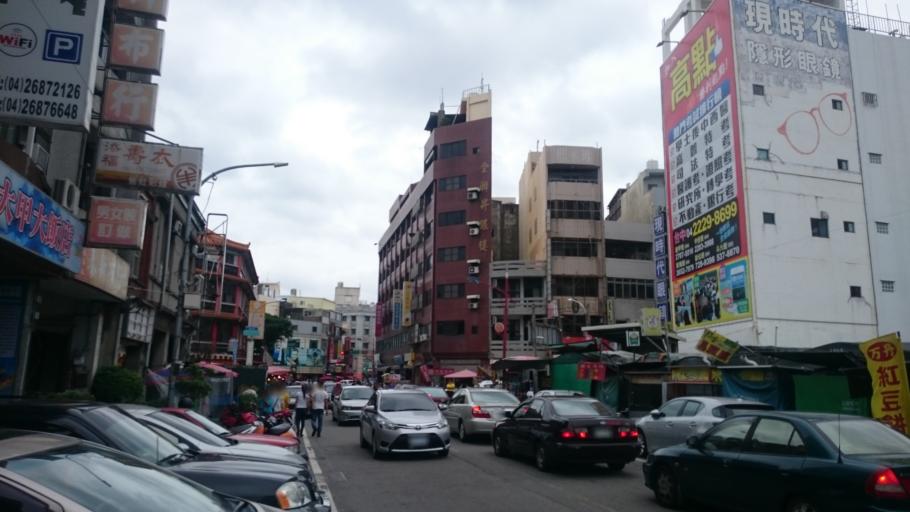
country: TW
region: Taiwan
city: Fengyuan
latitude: 24.3452
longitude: 120.6243
